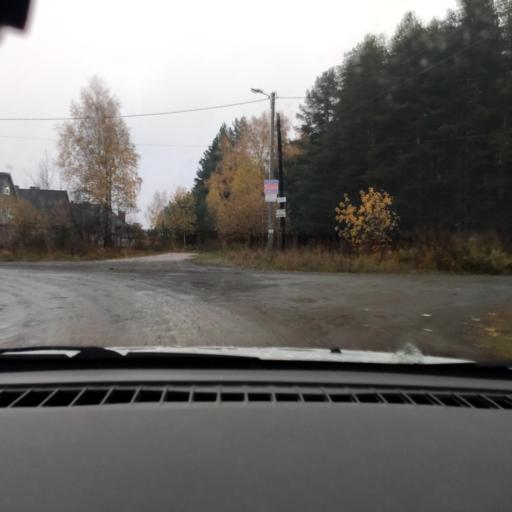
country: RU
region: Perm
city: Kondratovo
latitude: 58.0496
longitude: 56.1027
